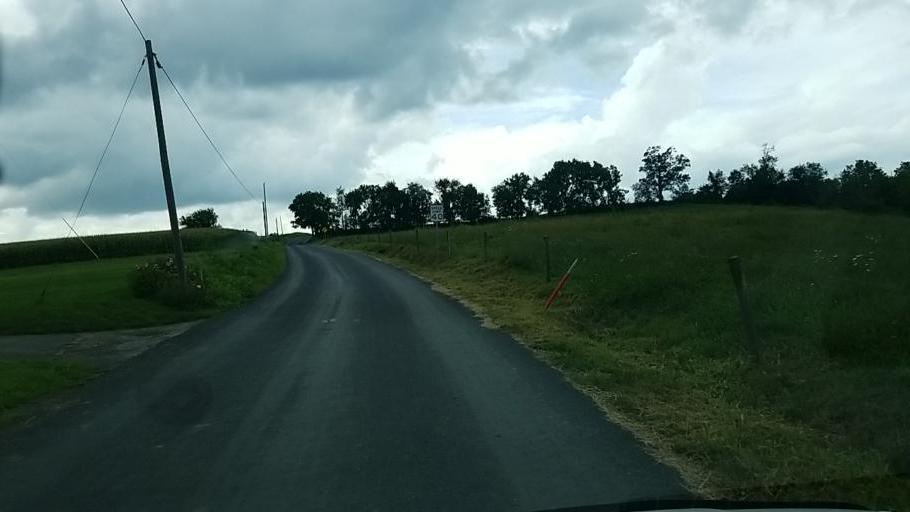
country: US
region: Pennsylvania
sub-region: Dauphin County
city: Elizabethville
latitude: 40.5741
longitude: -76.8471
